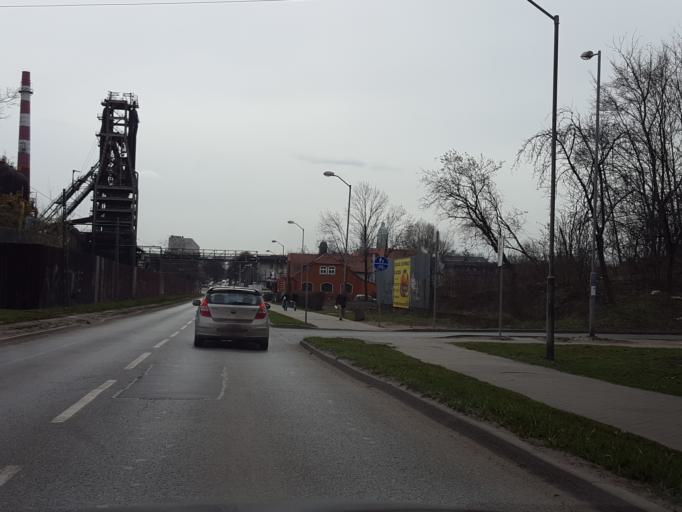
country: PL
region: Silesian Voivodeship
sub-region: Ruda Slaska
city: Ruda Slaska
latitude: 50.2929
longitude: 18.8738
